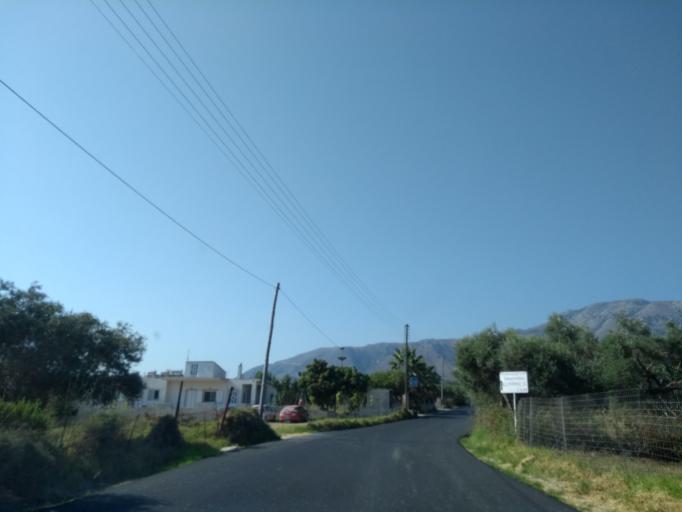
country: GR
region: Crete
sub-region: Nomos Chanias
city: Georgioupolis
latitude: 35.3375
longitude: 24.3020
